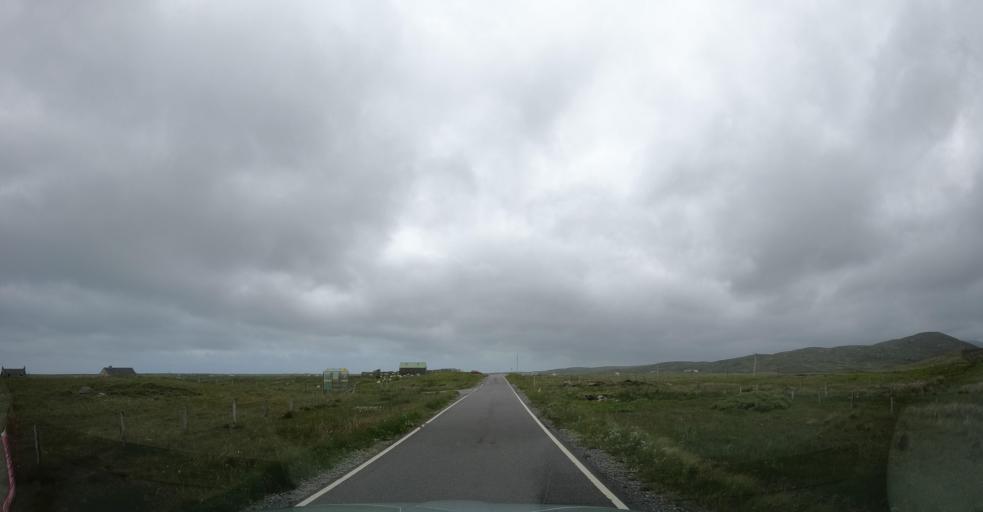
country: GB
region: Scotland
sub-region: Eilean Siar
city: Isle of South Uist
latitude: 57.2015
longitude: -7.3916
